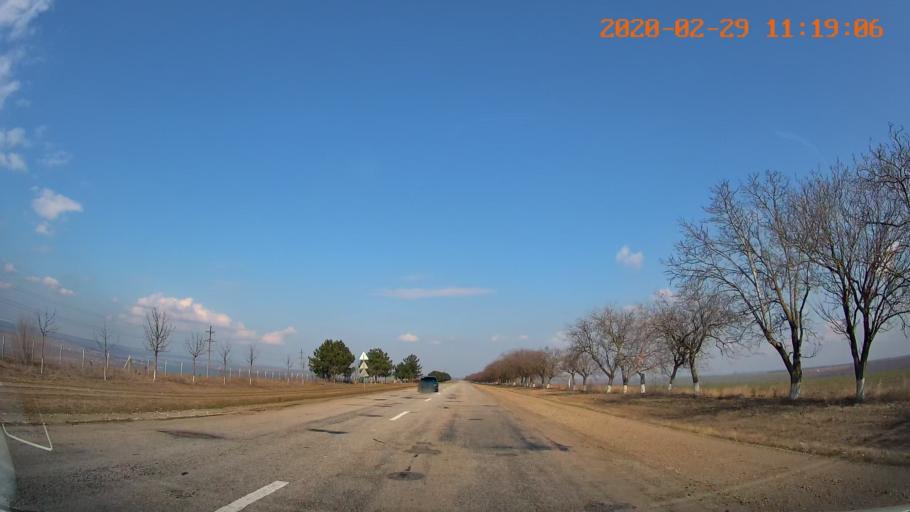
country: MD
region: Telenesti
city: Cocieri
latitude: 47.3448
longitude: 29.1757
